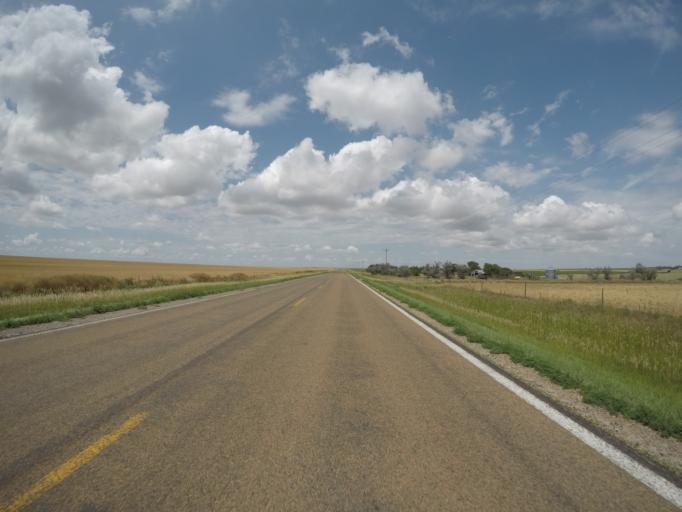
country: US
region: Kansas
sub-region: Rawlins County
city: Atwood
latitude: 39.8941
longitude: -101.0467
